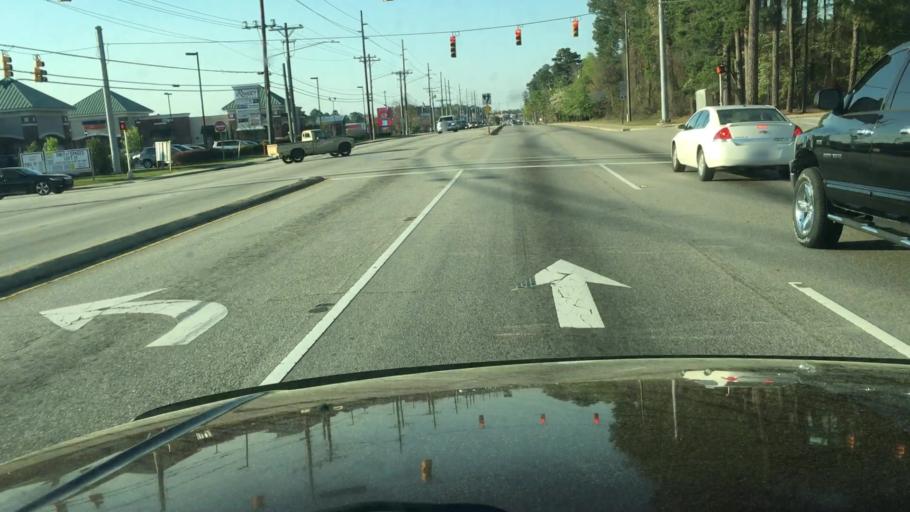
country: US
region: North Carolina
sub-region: Cumberland County
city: Fayetteville
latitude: 35.1201
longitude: -78.8797
